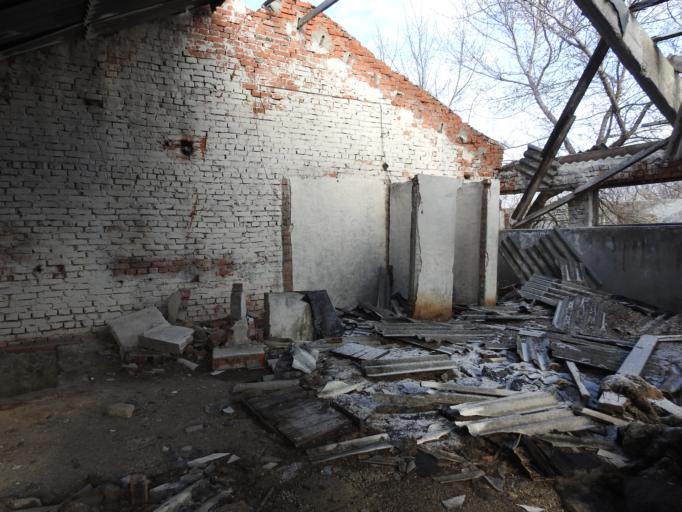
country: RU
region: Saratov
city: Krasnyy Oktyabr'
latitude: 51.3845
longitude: 45.6858
